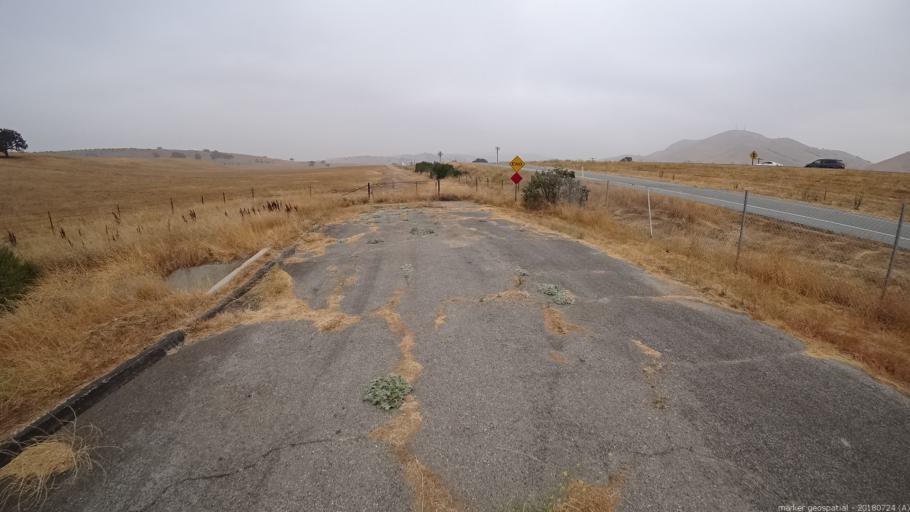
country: US
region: California
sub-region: San Luis Obispo County
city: Lake Nacimiento
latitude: 35.8649
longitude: -120.8196
